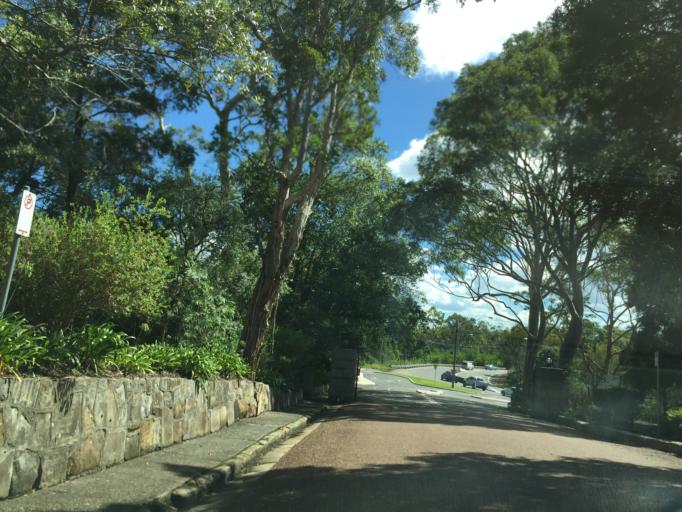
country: AU
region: New South Wales
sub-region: Willoughby
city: Chatswood West
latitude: -33.7948
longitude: 151.1521
